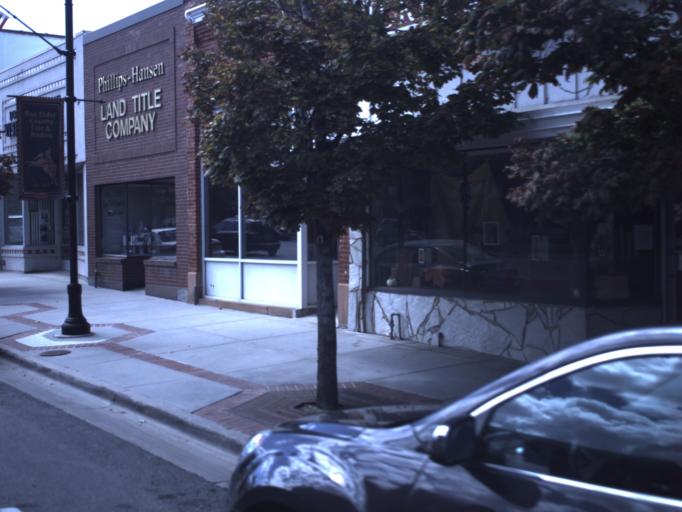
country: US
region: Utah
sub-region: Box Elder County
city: Brigham City
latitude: 41.5099
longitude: -112.0159
